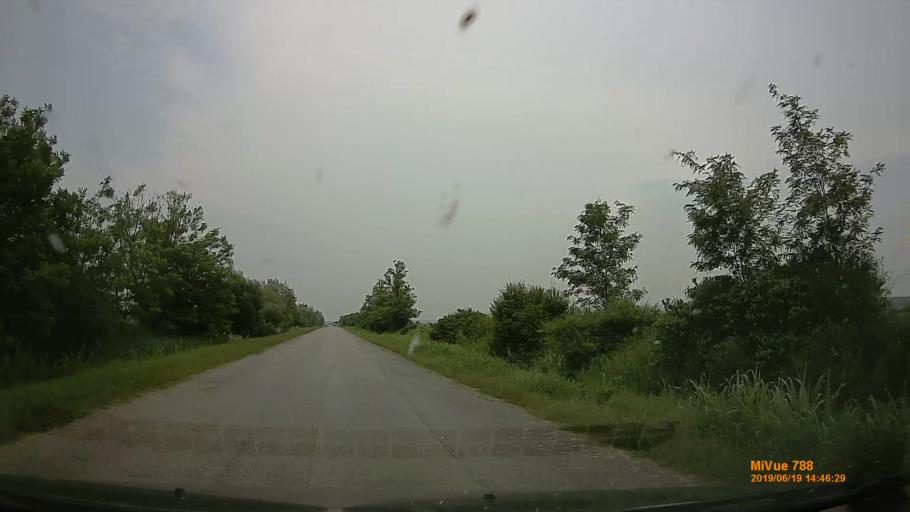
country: HU
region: Baranya
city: Szigetvar
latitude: 46.0064
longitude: 17.8246
